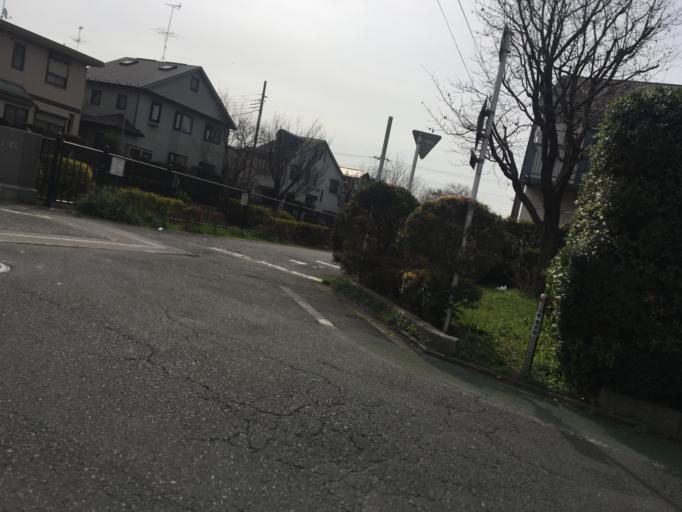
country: JP
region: Tokyo
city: Kokubunji
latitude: 35.6949
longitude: 139.4993
